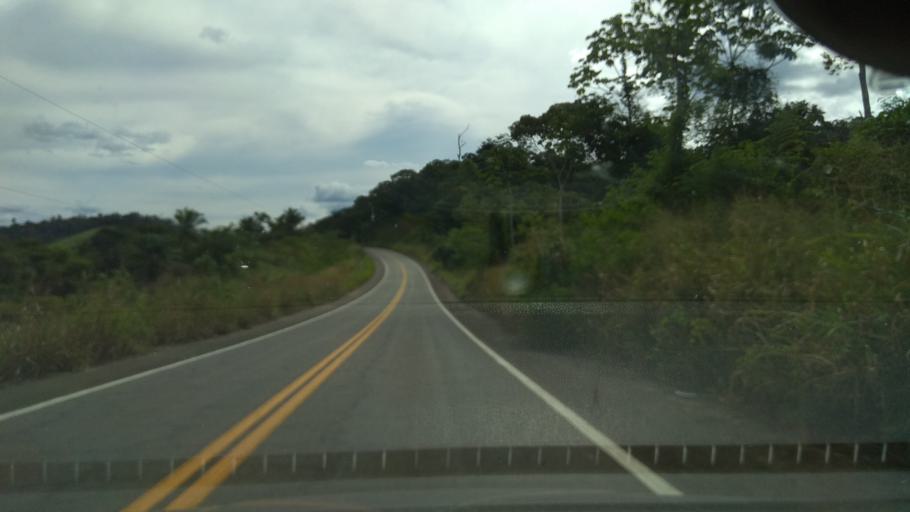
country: BR
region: Bahia
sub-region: Ubata
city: Ubata
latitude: -14.2278
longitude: -39.4609
